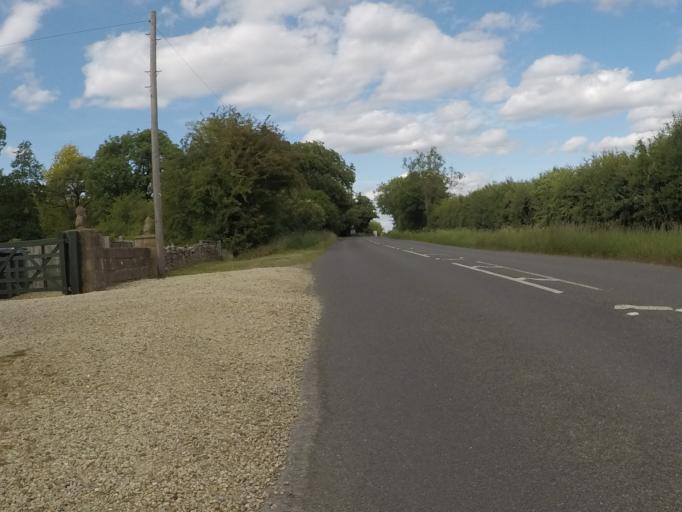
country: GB
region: England
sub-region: Oxfordshire
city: Charlbury
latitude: 51.8397
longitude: -1.4945
